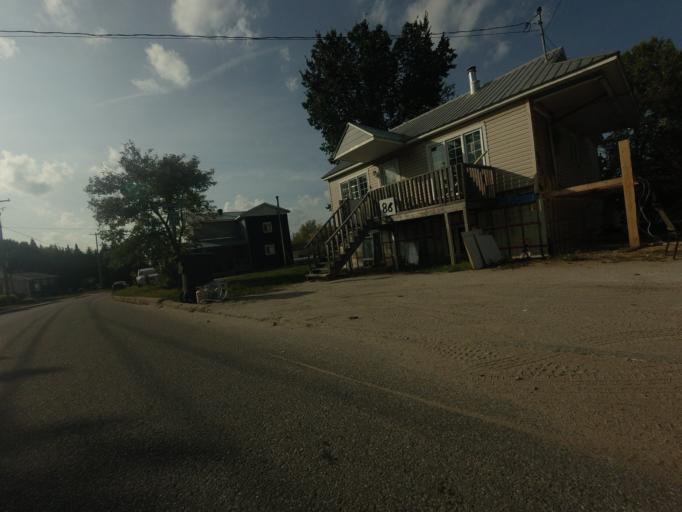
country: CA
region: Quebec
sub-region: Outaouais
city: Maniwaki
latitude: 46.3633
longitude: -75.9856
